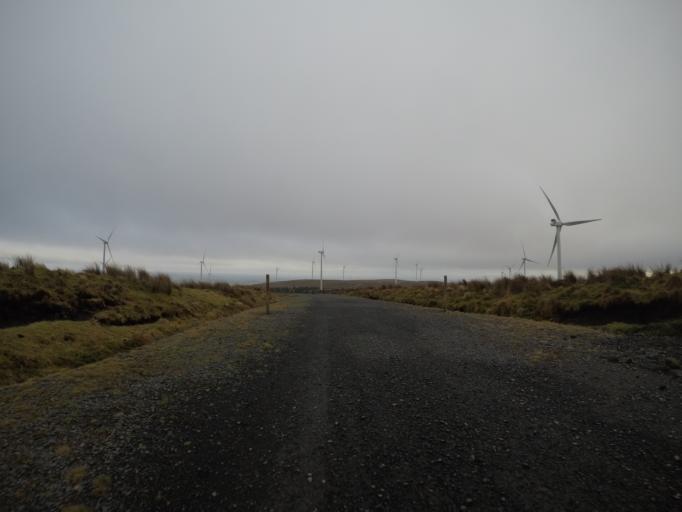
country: GB
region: Scotland
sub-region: North Ayrshire
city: Fairlie
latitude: 55.7428
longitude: -4.7915
